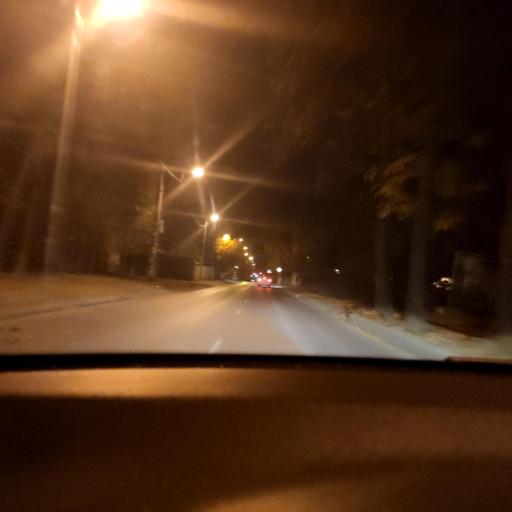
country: RU
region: Samara
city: Samara
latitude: 53.2389
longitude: 50.2595
